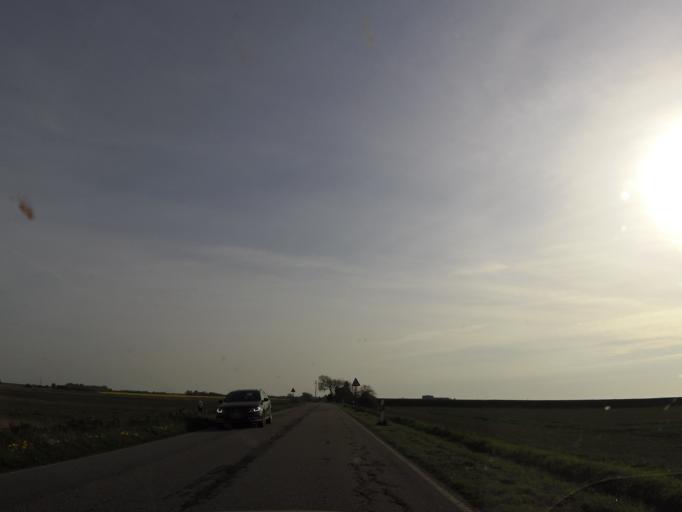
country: DE
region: Schleswig-Holstein
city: Galmsbull
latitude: 54.7426
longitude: 8.7279
